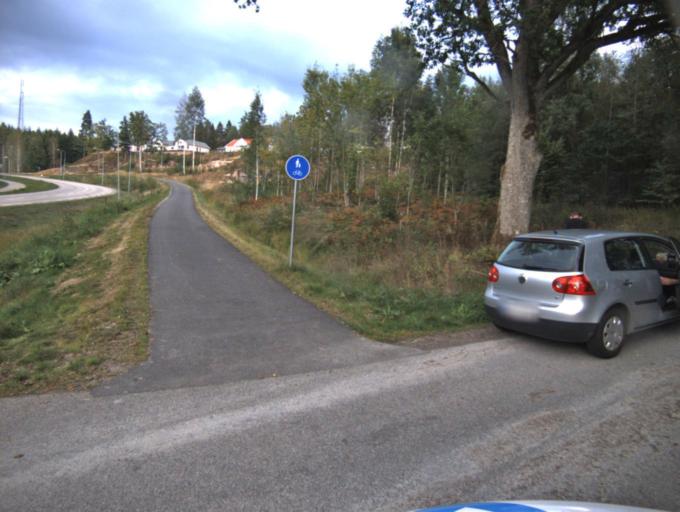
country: SE
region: Vaestra Goetaland
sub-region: Ulricehamns Kommun
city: Ulricehamn
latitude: 57.7735
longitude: 13.4096
